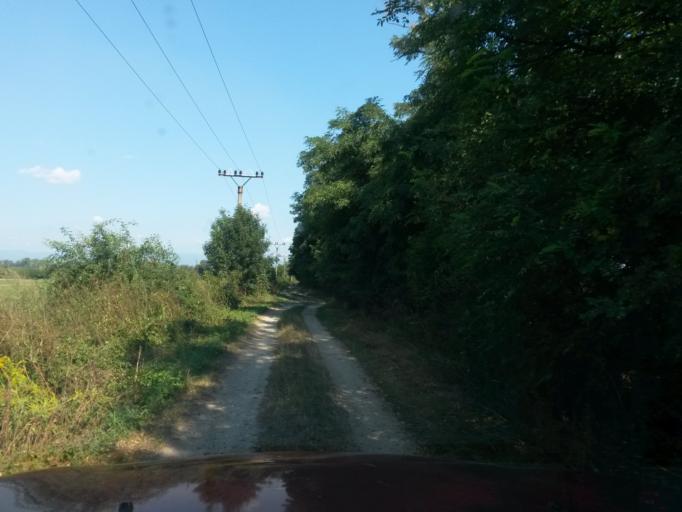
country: HU
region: Borsod-Abauj-Zemplen
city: Gonc
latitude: 48.5351
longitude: 21.1571
